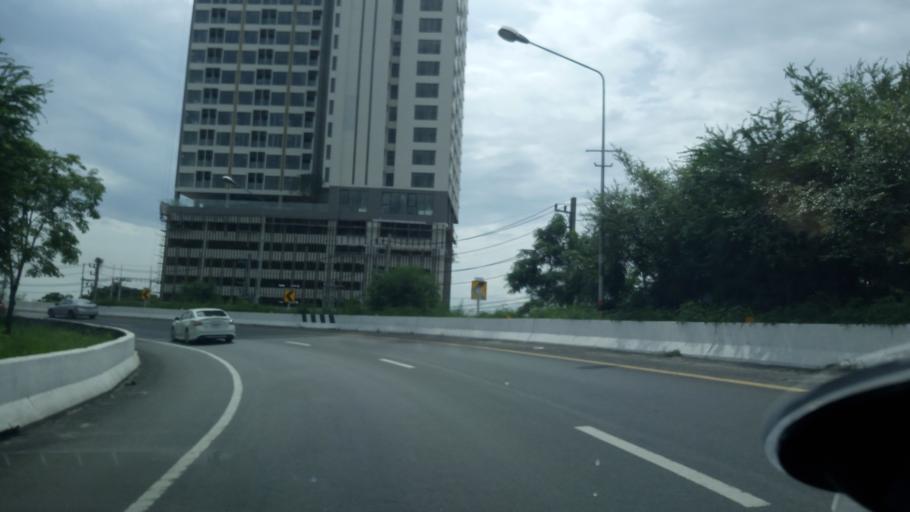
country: TH
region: Chon Buri
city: Chon Buri
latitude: 13.3348
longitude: 100.9694
